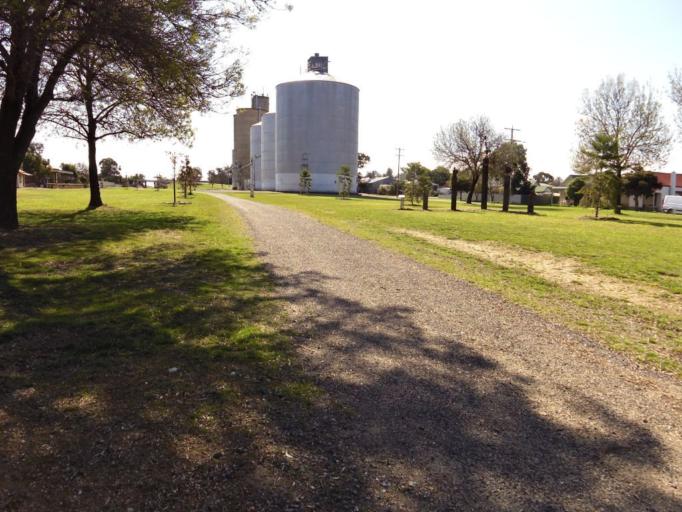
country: AU
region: New South Wales
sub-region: Corowa Shire
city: Corowa
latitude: -36.0553
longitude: 146.4637
